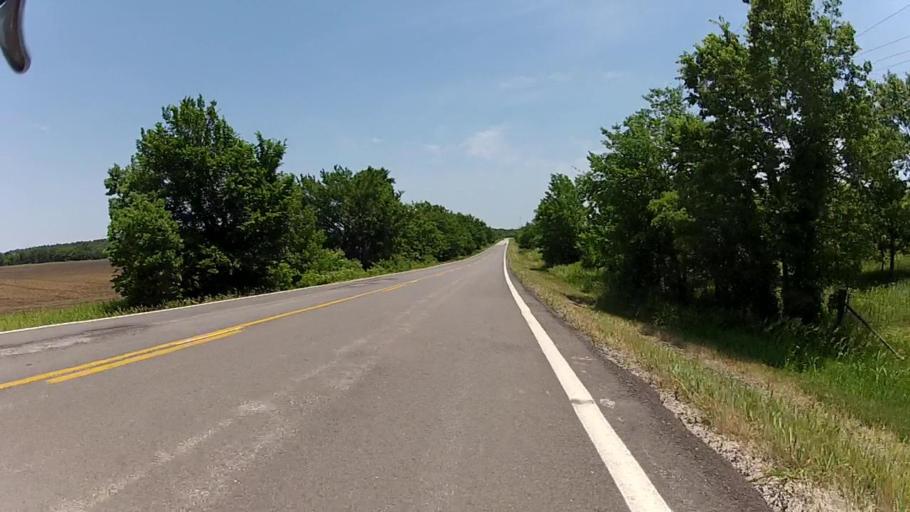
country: US
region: Kansas
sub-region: Chautauqua County
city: Sedan
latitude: 37.1201
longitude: -96.2315
